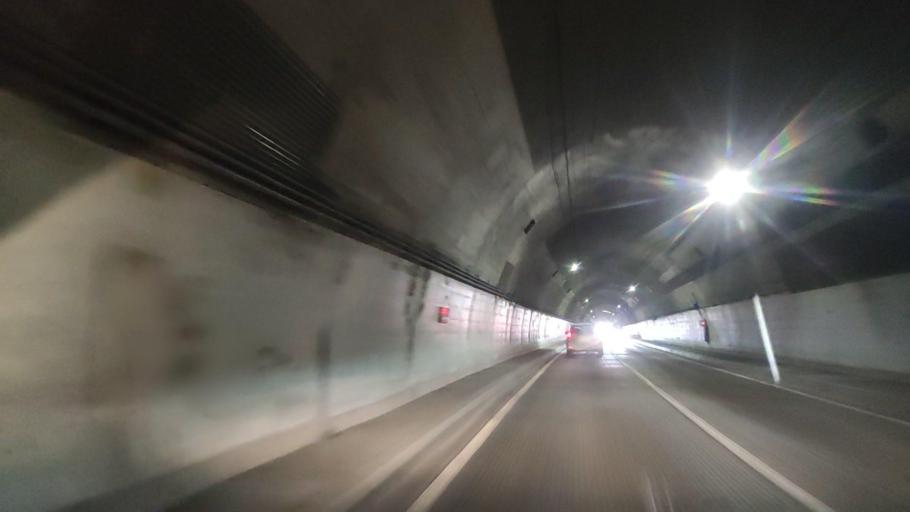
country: JP
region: Hokkaido
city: Ishikari
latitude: 43.4432
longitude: 141.4135
